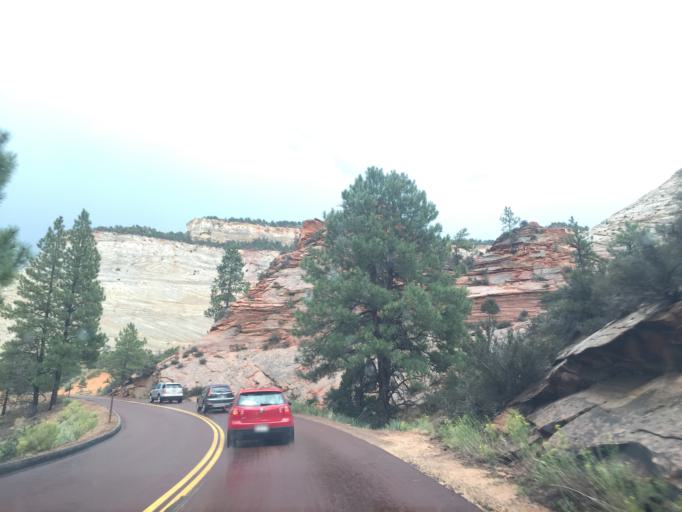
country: US
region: Utah
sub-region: Washington County
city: Hildale
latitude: 37.2258
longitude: -112.8891
